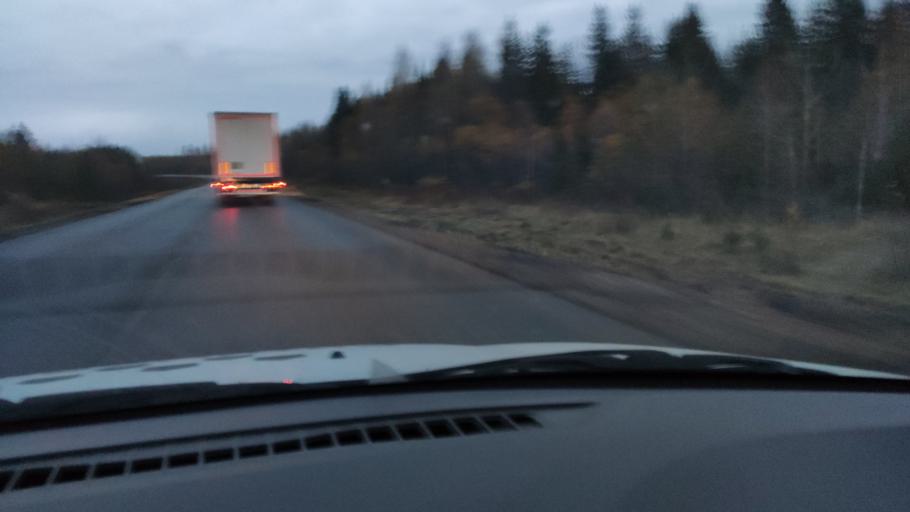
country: RU
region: Kirov
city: Kostino
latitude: 58.8173
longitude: 53.3244
